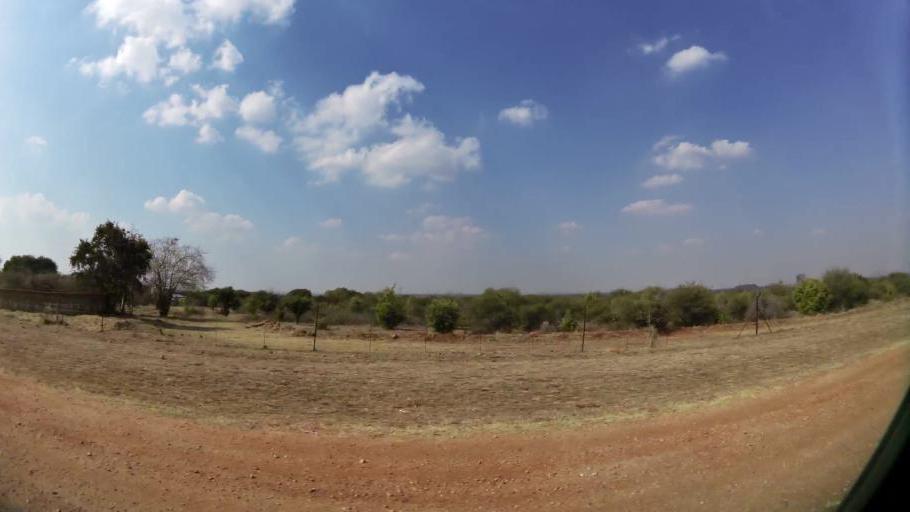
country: ZA
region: North-West
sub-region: Bojanala Platinum District Municipality
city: Mogwase
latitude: -25.4732
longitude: 27.0870
